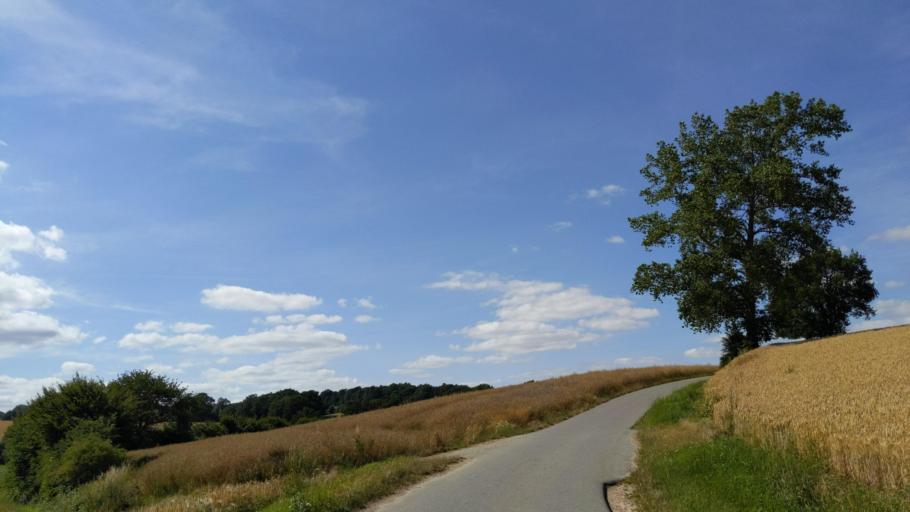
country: DE
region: Schleswig-Holstein
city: Kasseedorf
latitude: 54.1385
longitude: 10.7379
